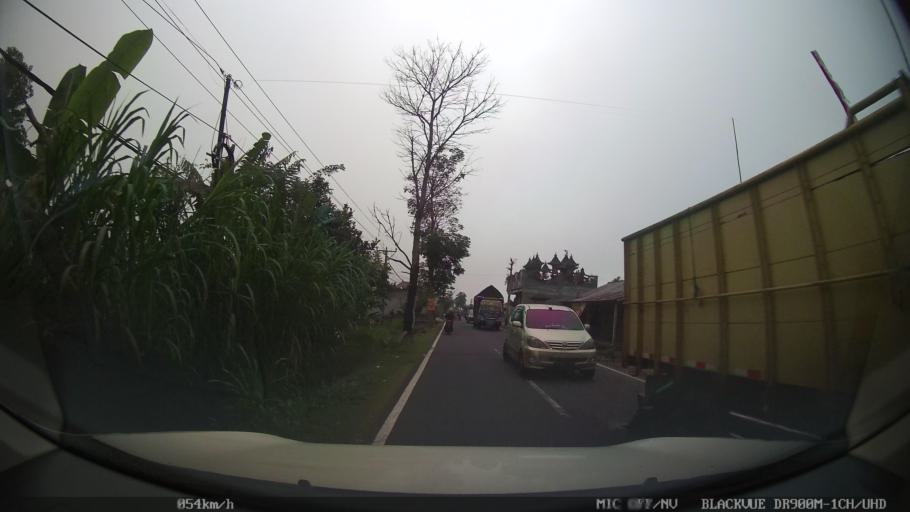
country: ID
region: Bali
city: Banjar Kedisan
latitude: -8.3004
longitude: 115.3095
